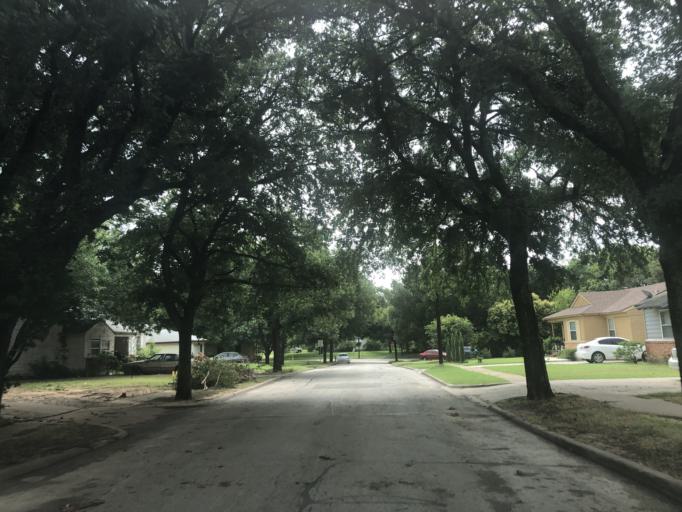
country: US
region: Texas
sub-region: Dallas County
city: Irving
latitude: 32.8060
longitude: -96.9615
